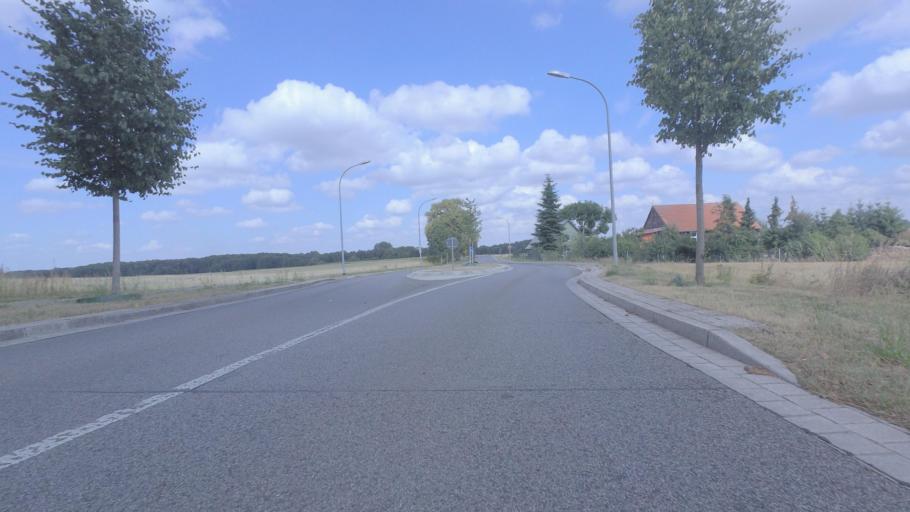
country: DE
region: Brandenburg
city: Walsleben
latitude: 52.9919
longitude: 12.6536
